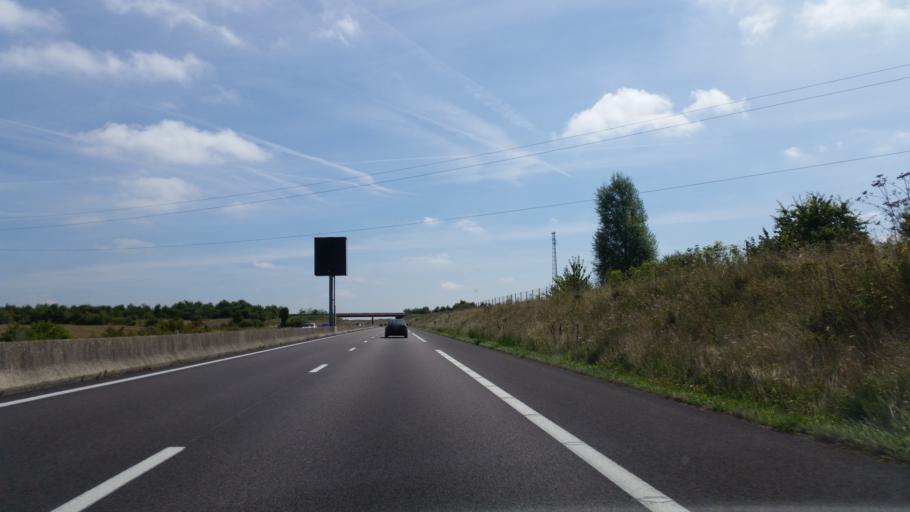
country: FR
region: Haute-Normandie
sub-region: Departement de la Seine-Maritime
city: Gaillefontaine
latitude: 49.7399
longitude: 1.6048
